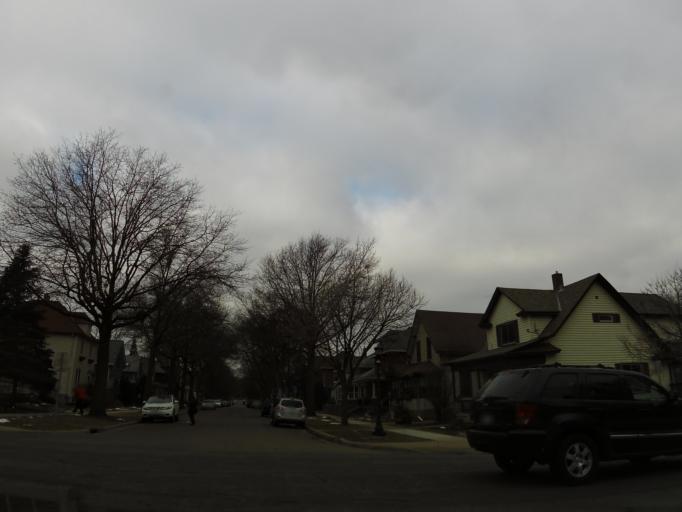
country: US
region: Minnesota
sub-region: Dakota County
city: West Saint Paul
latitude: 44.9278
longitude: -93.1363
